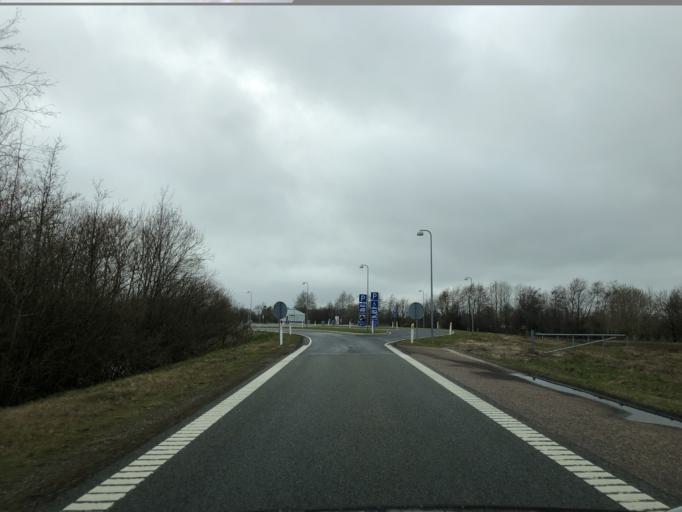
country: DK
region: North Denmark
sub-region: Bronderslev Kommune
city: Hjallerup
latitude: 57.1542
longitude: 10.1602
